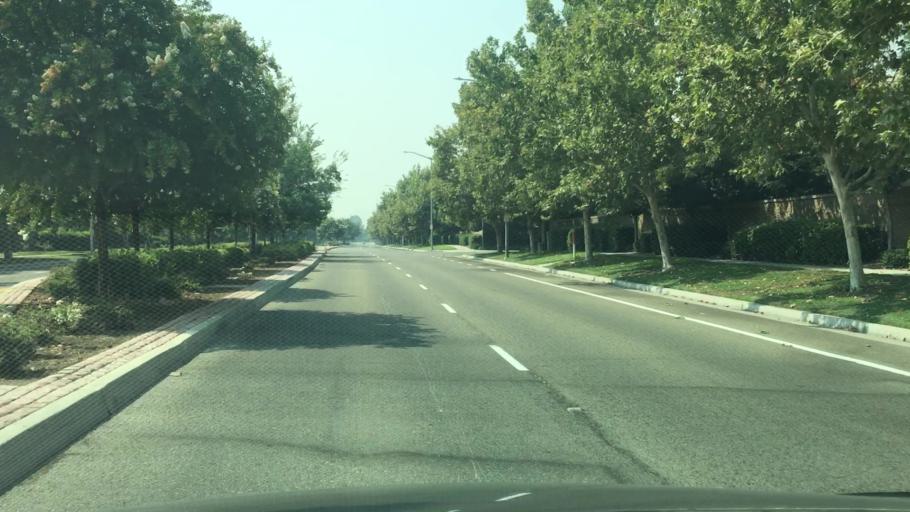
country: US
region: California
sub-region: Fresno County
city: Clovis
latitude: 36.8657
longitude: -119.7022
